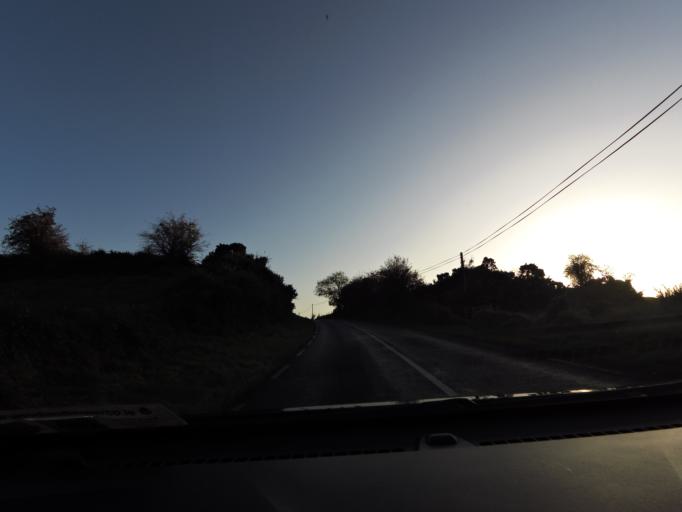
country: IE
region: Connaught
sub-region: Roscommon
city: Castlerea
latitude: 53.7019
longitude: -8.5677
